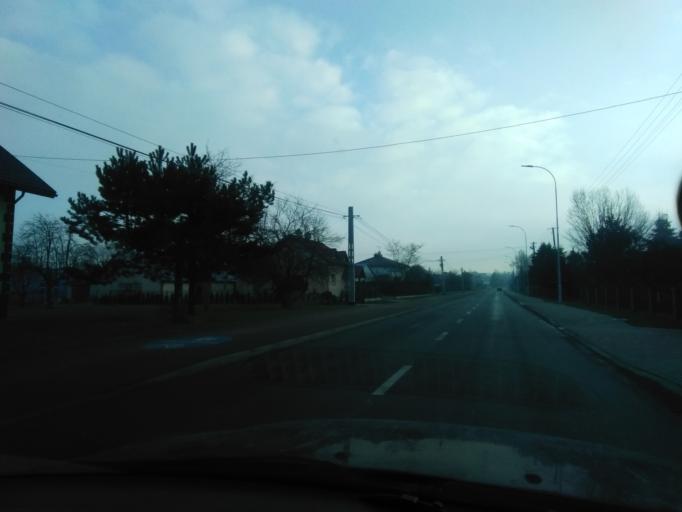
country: PL
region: Subcarpathian Voivodeship
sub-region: Powiat rzeszowski
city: Tyczyn
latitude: 49.9761
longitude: 21.9934
